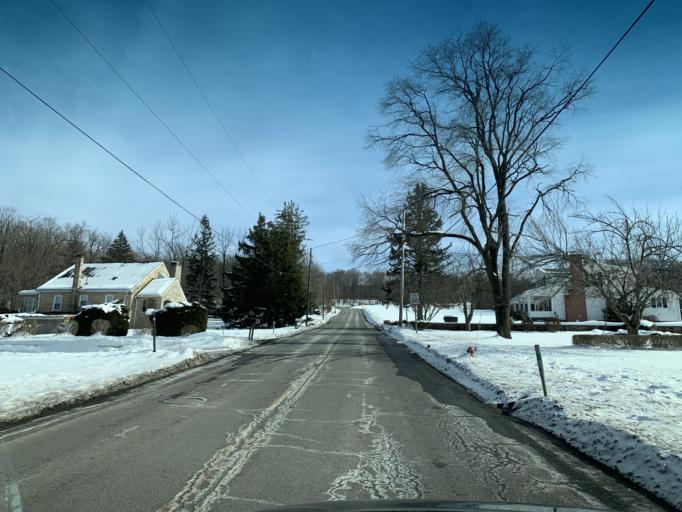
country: US
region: Maryland
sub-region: Allegany County
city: Frostburg
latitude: 39.6765
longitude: -78.8952
